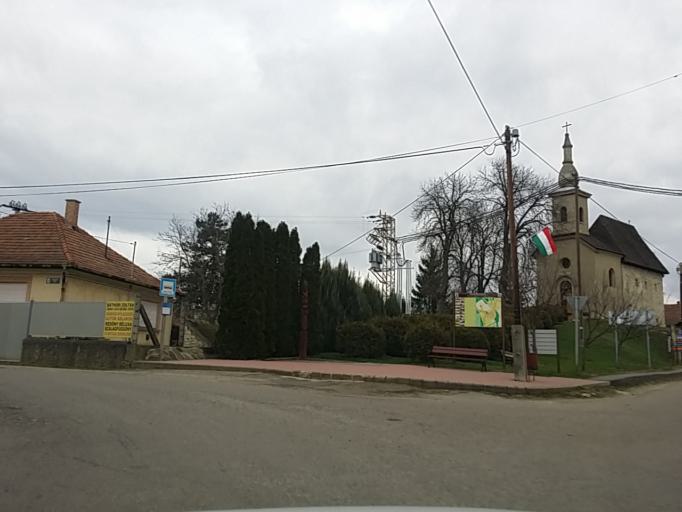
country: HU
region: Heves
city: Verpelet
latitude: 47.8773
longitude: 20.2015
